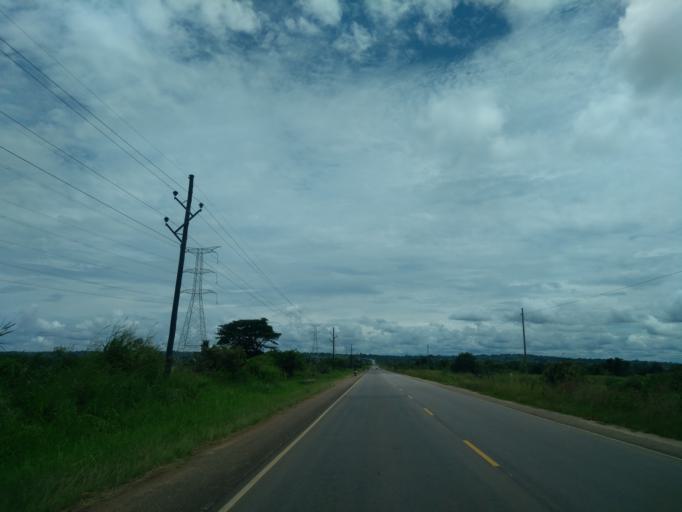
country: UG
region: Central Region
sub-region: Butambala District
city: Gombe
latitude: -0.0249
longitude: 32.0202
